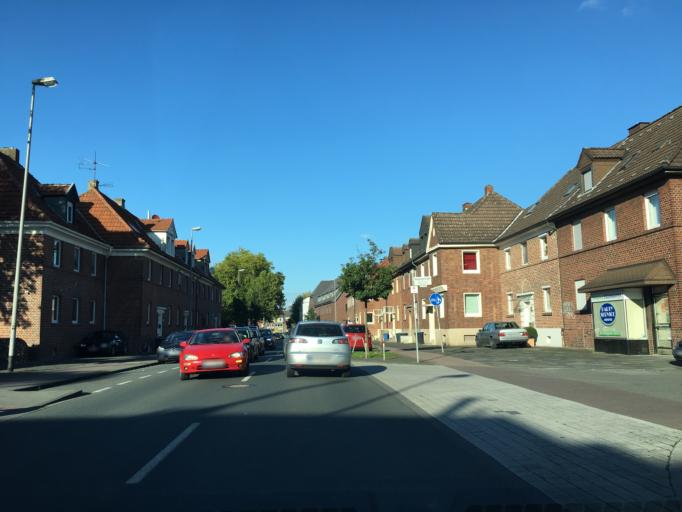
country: DE
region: North Rhine-Westphalia
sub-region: Regierungsbezirk Munster
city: Muenster
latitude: 51.9703
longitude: 7.6347
